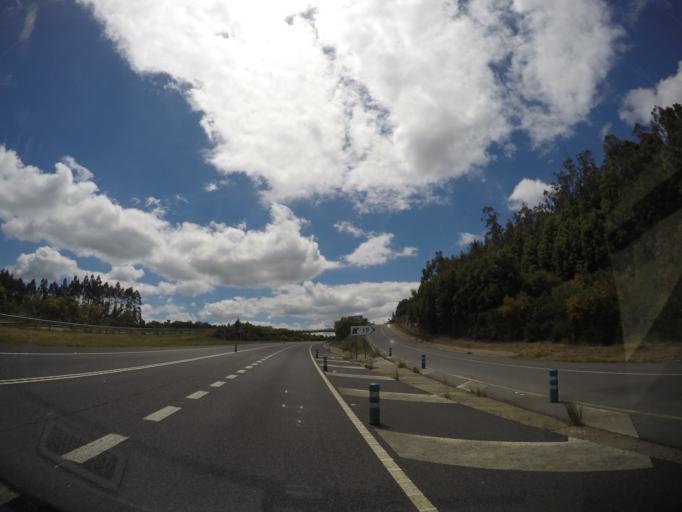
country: ES
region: Aragon
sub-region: Provincia de Zaragoza
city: Fuentes de Ebro
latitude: 41.4976
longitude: -0.6508
